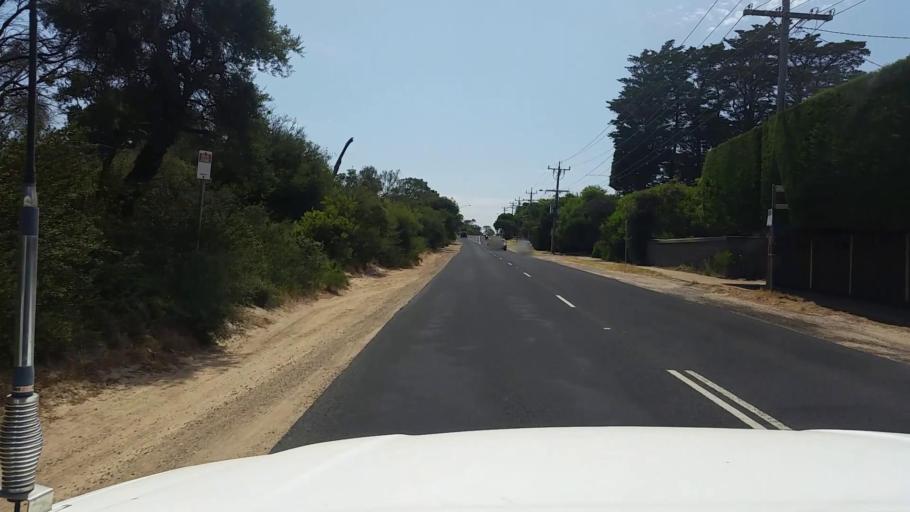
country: AU
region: Victoria
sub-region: Mornington Peninsula
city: Mount Martha
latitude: -38.2560
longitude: 145.0249
